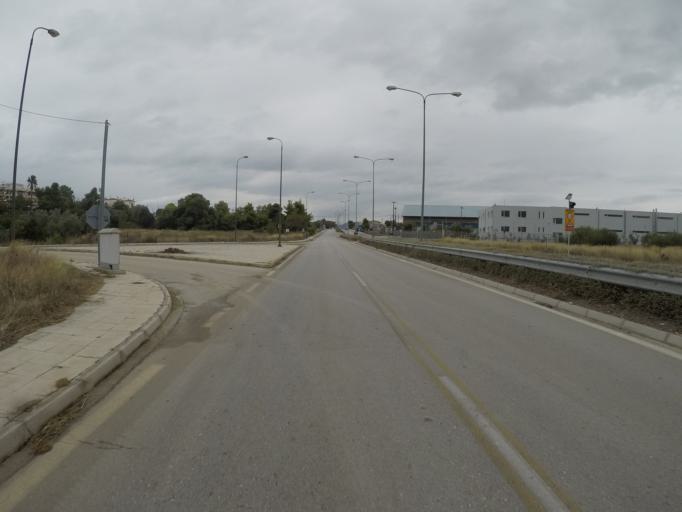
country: GR
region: Peloponnese
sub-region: Nomos Korinthias
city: Korinthos
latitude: 37.9466
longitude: 22.9794
